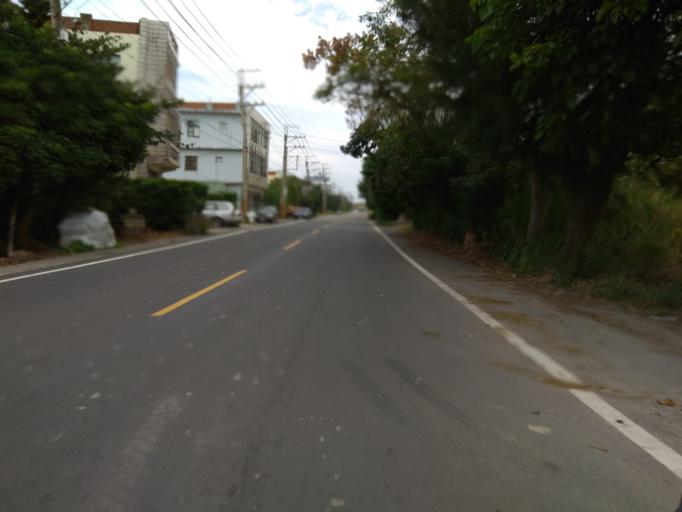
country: TW
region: Taiwan
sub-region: Hsinchu
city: Zhubei
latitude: 24.9838
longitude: 121.0409
